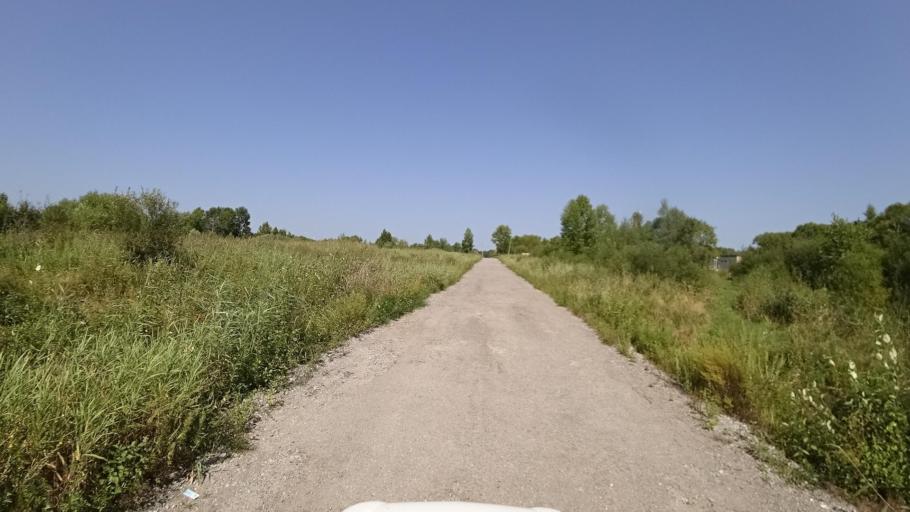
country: RU
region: Khabarovsk Krai
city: Khor
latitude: 47.9659
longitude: 135.1132
